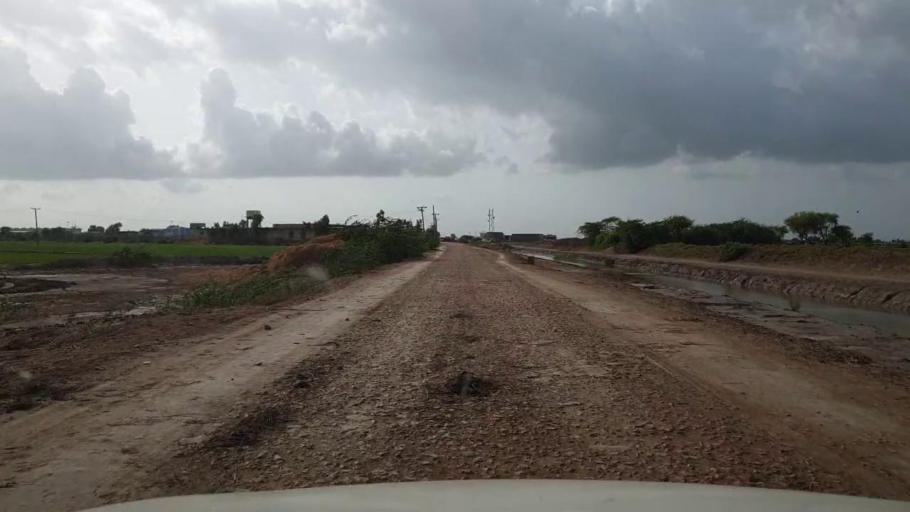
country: PK
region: Sindh
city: Kario
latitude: 24.7928
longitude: 68.5780
